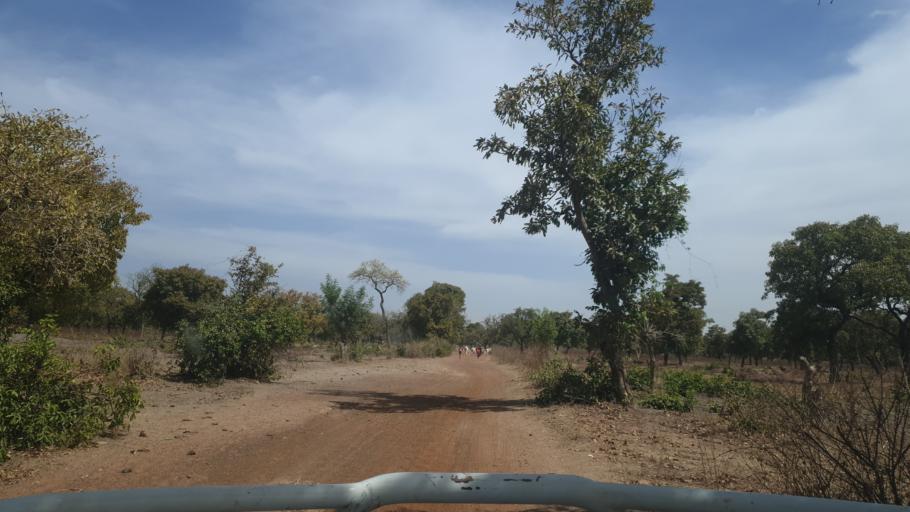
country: ML
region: Sikasso
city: Yorosso
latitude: 12.2727
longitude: -4.6934
